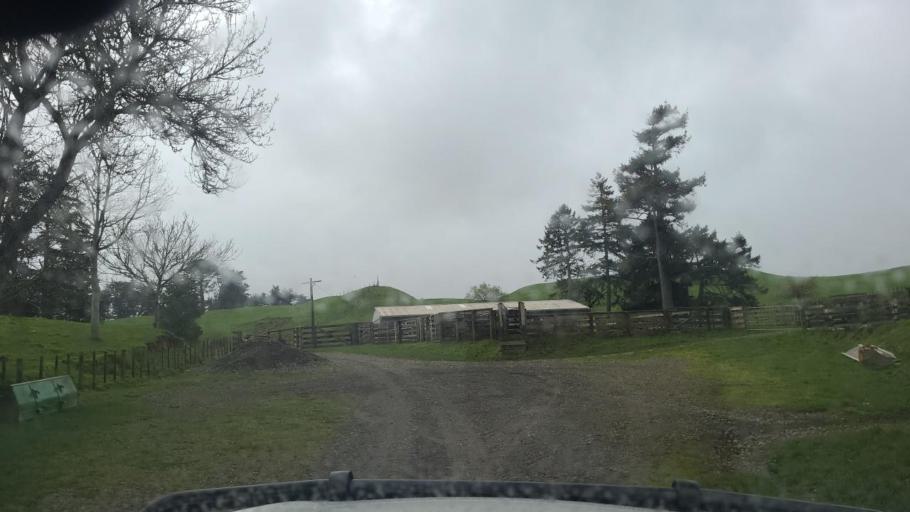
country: NZ
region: Taranaki
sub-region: South Taranaki District
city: Eltham
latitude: -39.2474
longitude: 174.4120
